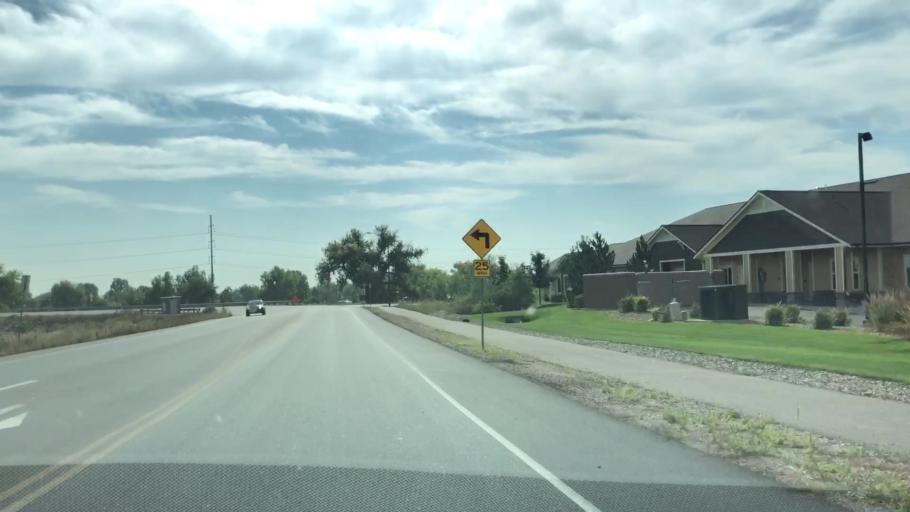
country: US
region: Colorado
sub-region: Larimer County
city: Loveland
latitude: 40.4286
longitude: -105.0481
